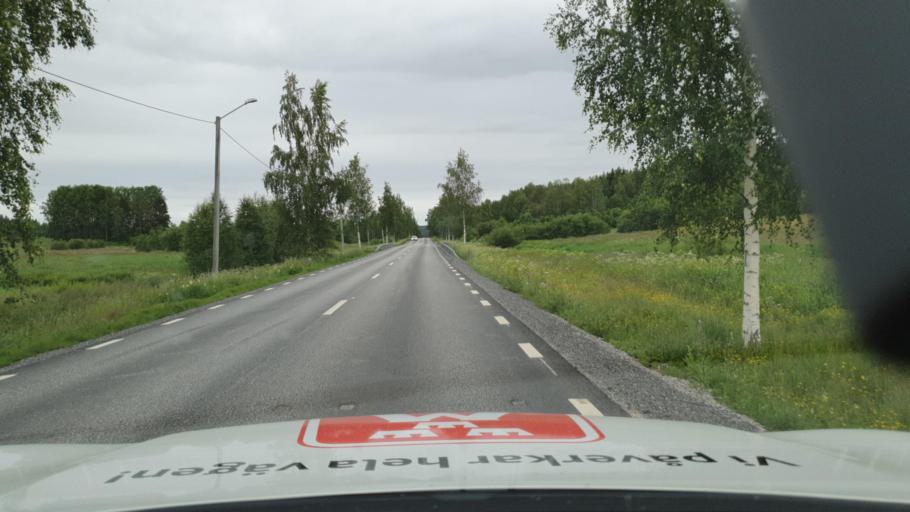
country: SE
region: Vaesterbotten
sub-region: Vannas Kommun
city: Vaennaes
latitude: 63.7528
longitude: 19.6394
